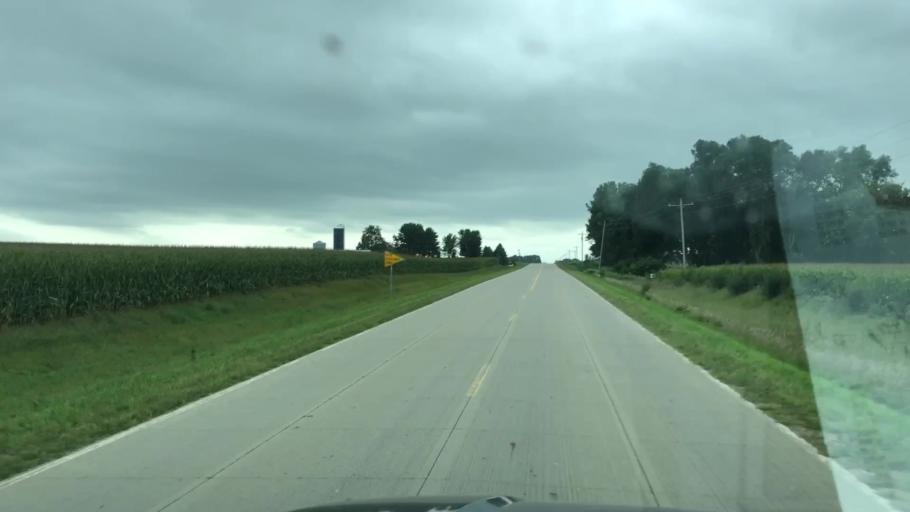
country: US
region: Iowa
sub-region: Sioux County
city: Alton
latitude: 43.0955
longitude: -95.9784
